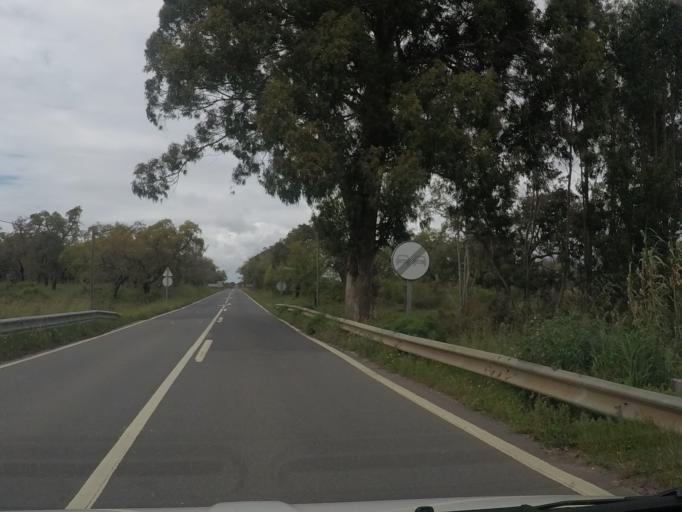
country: PT
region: Setubal
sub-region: Santiago do Cacem
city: Cercal
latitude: 37.8518
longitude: -8.7109
